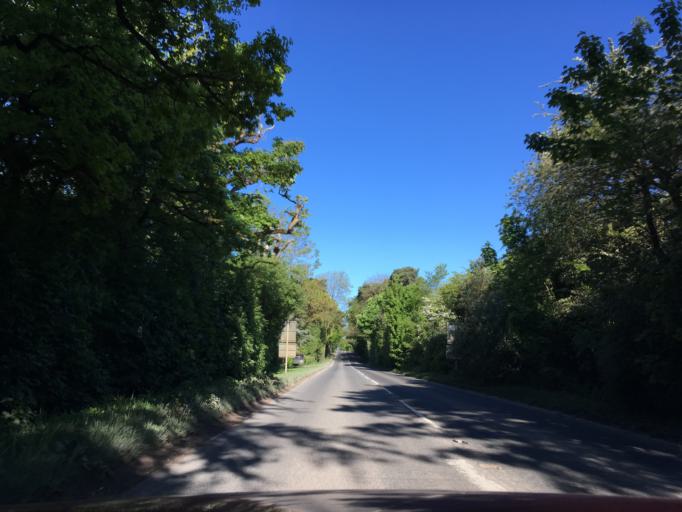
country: GB
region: England
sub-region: North Somerset
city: Long Ashton
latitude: 51.4379
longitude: -2.6701
